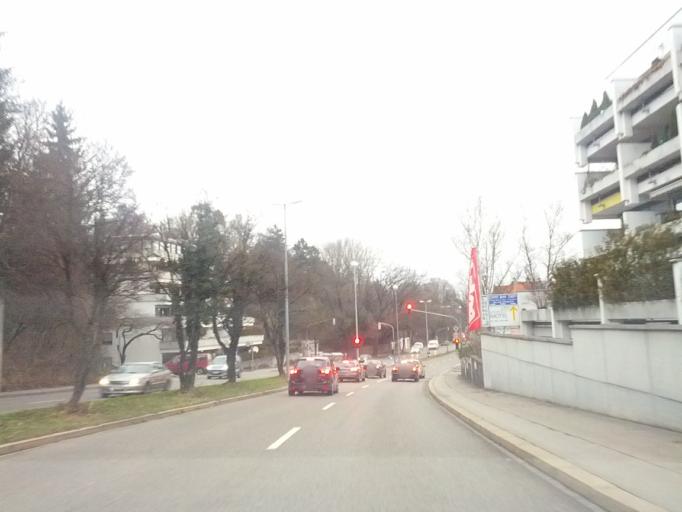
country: DE
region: Bavaria
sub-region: Swabia
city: Kempten (Allgaeu)
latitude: 47.7232
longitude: 10.3022
